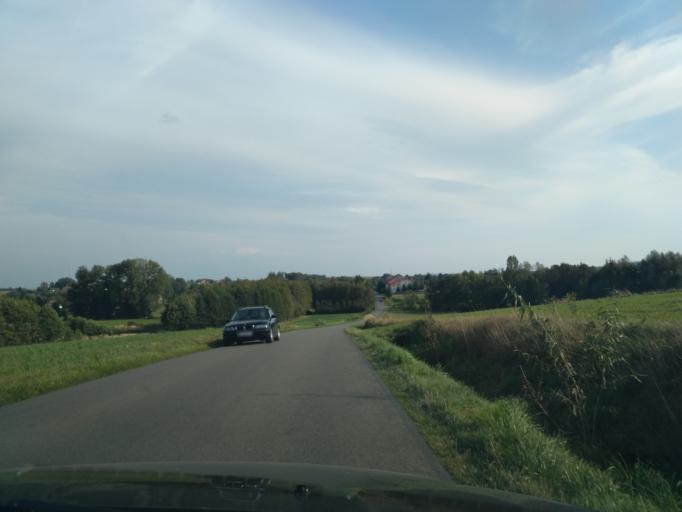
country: PL
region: Subcarpathian Voivodeship
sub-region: Powiat rzeszowski
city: Niechobrz
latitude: 49.9999
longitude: 21.8713
